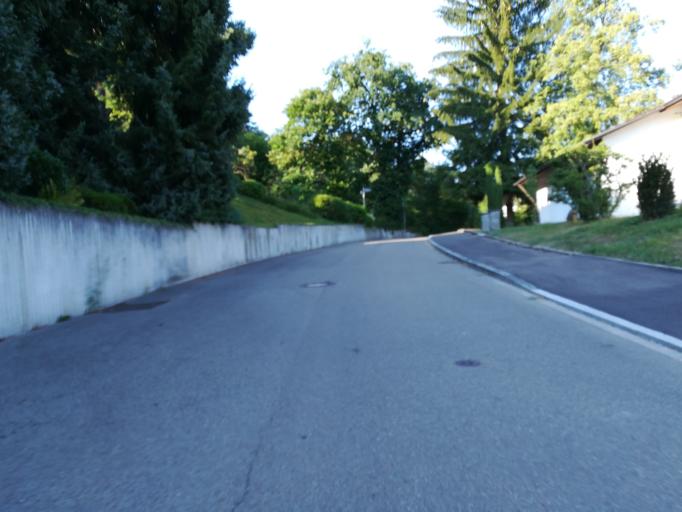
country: DE
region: Baden-Wuerttemberg
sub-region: Freiburg Region
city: Singen
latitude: 47.7585
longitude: 8.8175
